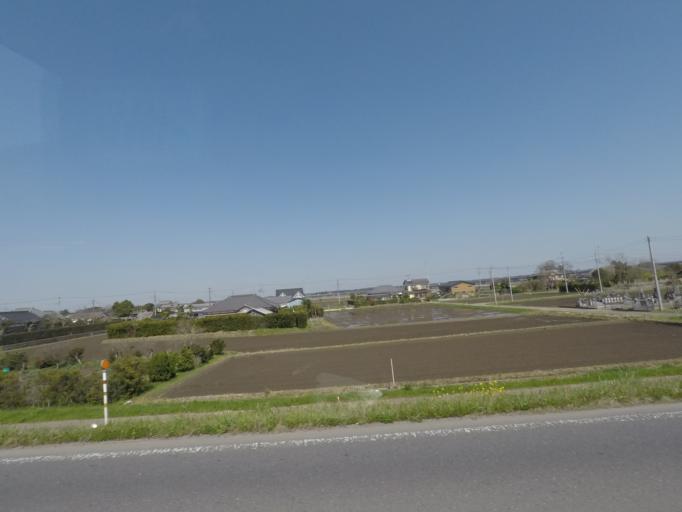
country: JP
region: Ibaraki
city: Inashiki
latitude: 35.9033
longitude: 140.3702
